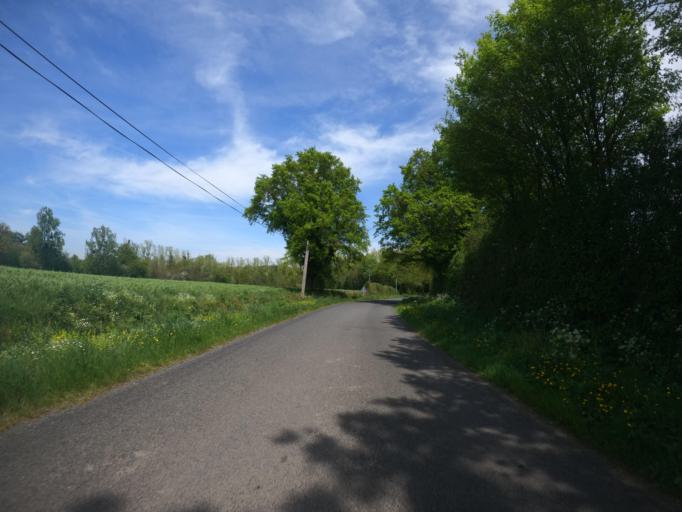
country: FR
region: Poitou-Charentes
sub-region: Departement des Deux-Sevres
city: La Chapelle-Saint-Laurent
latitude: 46.6681
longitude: -0.5054
